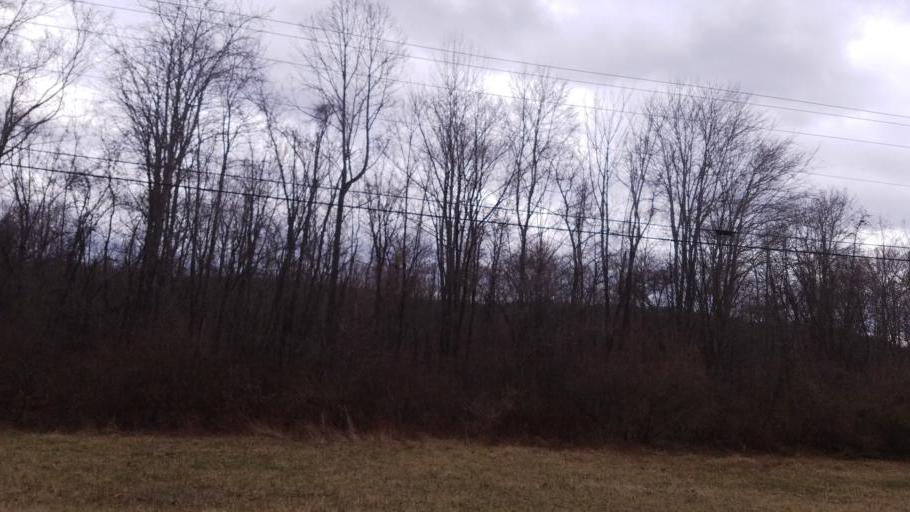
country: US
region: Ohio
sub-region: Muskingum County
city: Frazeysburg
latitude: 40.0690
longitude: -82.1585
